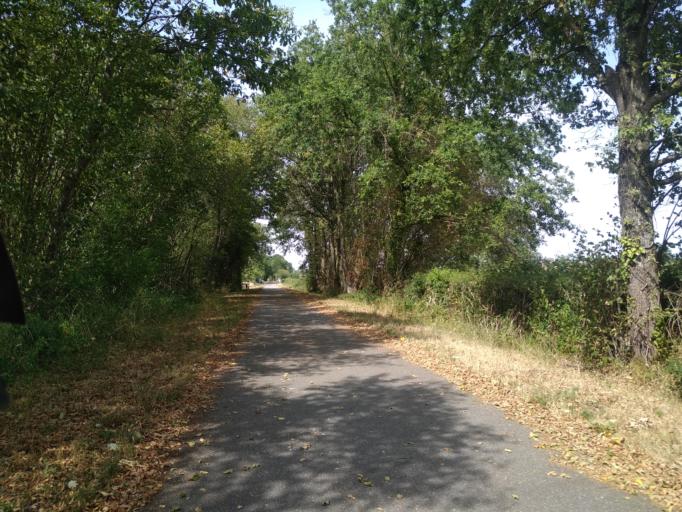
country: FR
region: Auvergne
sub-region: Departement de l'Allier
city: Diou
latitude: 46.5598
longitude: 3.7466
